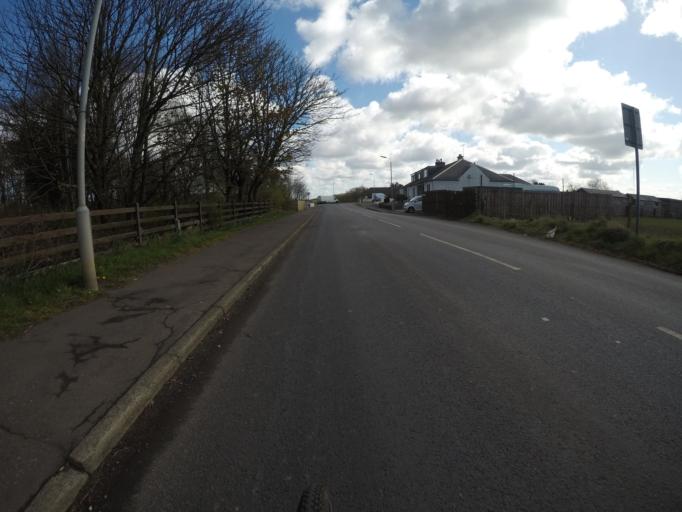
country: GB
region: Scotland
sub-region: North Ayrshire
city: Dreghorn
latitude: 55.5953
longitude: -4.6062
